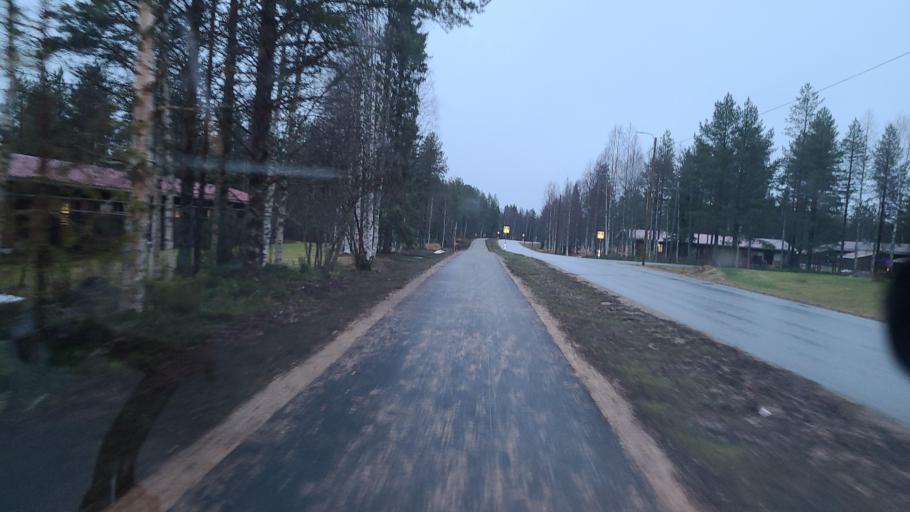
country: FI
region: Lapland
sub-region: Rovaniemi
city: Ranua
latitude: 65.9288
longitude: 26.4944
